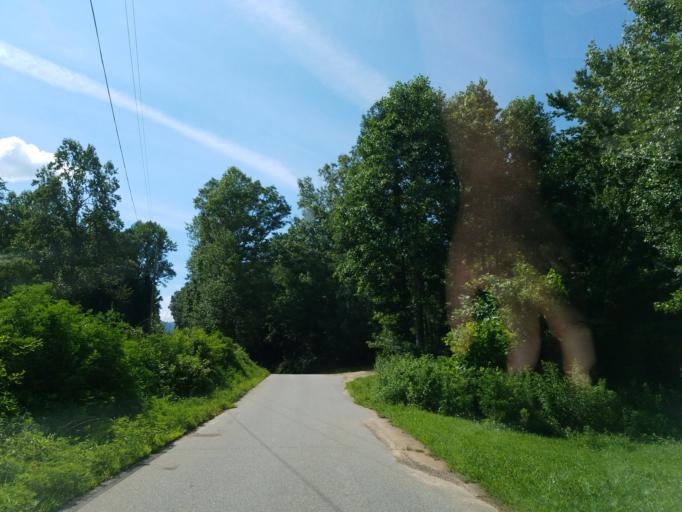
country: US
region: Georgia
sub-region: Dawson County
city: Dawsonville
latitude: 34.5641
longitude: -84.1428
